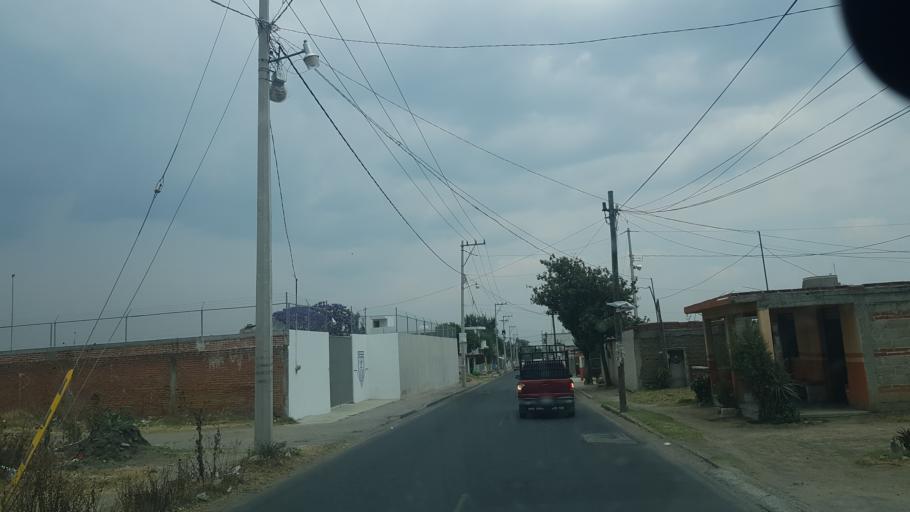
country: MX
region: Puebla
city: San Lorenzo Chiautzingo
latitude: 19.1975
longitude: -98.4431
